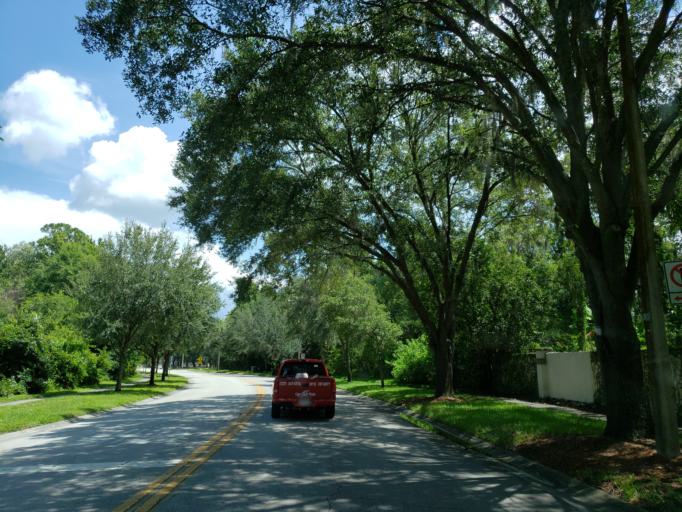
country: US
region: Florida
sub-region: Hillsborough County
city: Bloomingdale
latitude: 27.8898
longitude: -82.2469
